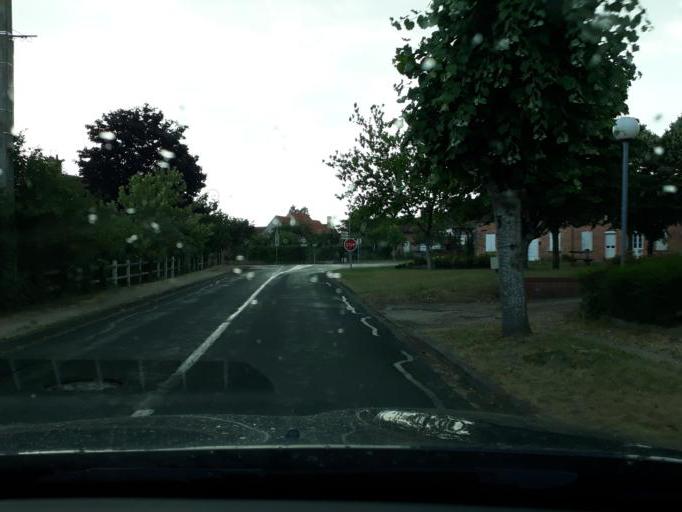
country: FR
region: Centre
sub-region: Departement du Loiret
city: Marcilly-en-Villette
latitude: 47.7647
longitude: 2.0253
